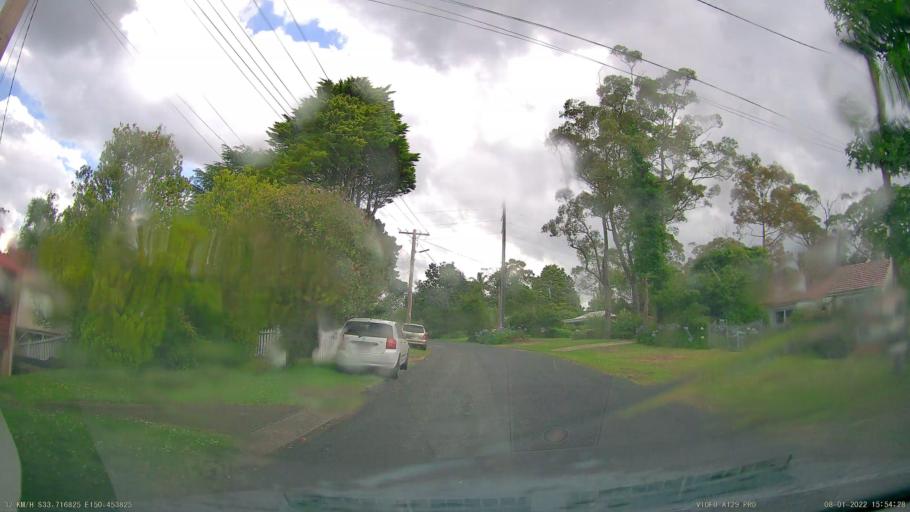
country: AU
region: New South Wales
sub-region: Blue Mountains Municipality
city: Hazelbrook
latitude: -33.7169
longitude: 150.4538
